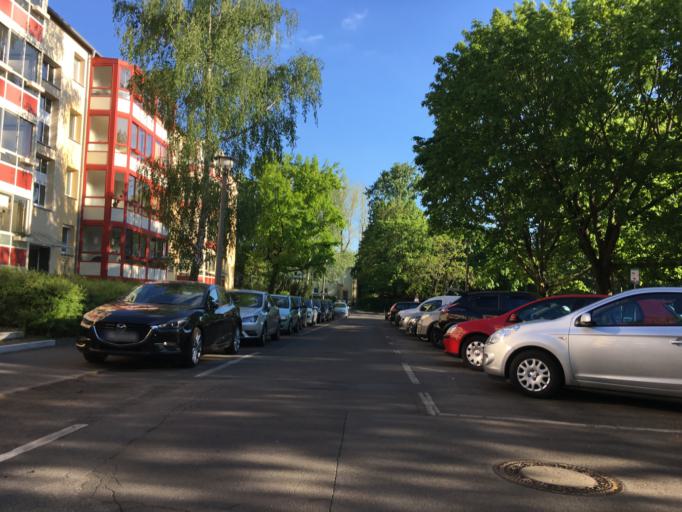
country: DE
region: Berlin
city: Weissensee
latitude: 52.5578
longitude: 13.4719
